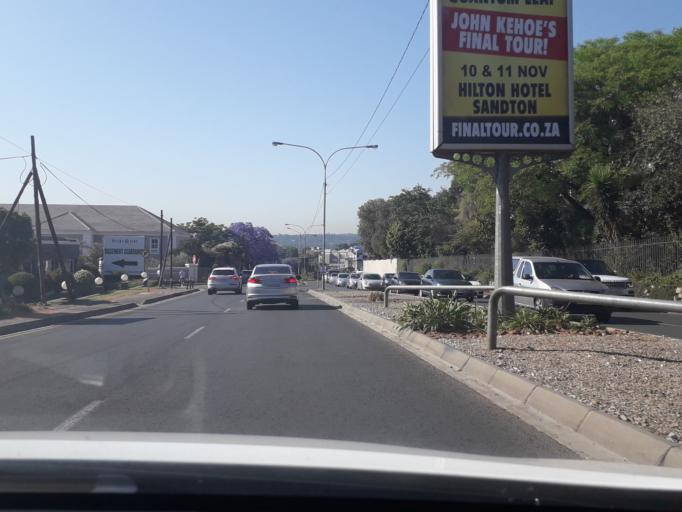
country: ZA
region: Gauteng
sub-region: City of Johannesburg Metropolitan Municipality
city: Johannesburg
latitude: -26.1252
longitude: 28.0488
